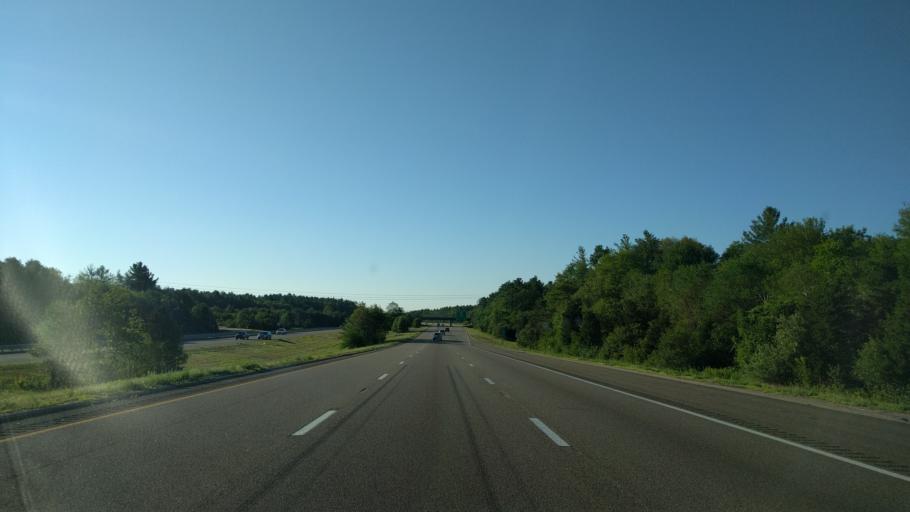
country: US
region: Massachusetts
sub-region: Bristol County
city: Mansfield Center
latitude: 42.0101
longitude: -71.2299
